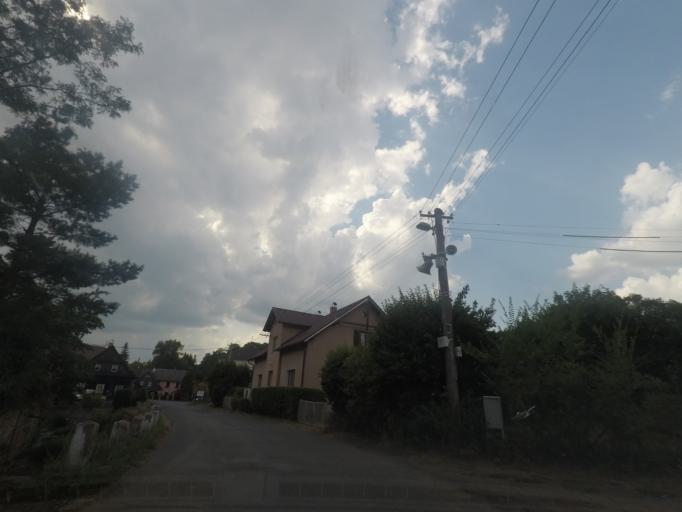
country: CZ
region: Ustecky
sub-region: Okres Decin
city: Chribska
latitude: 50.8663
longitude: 14.4713
